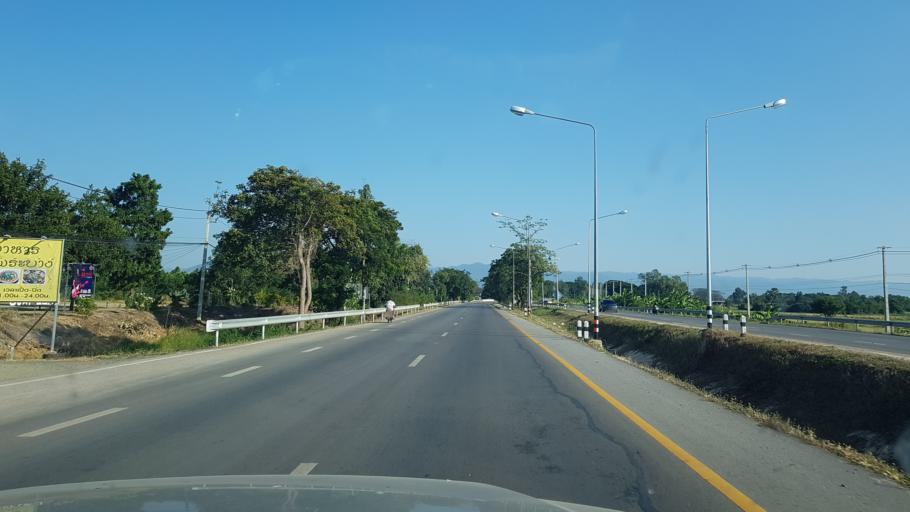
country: TH
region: Phetchabun
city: Lom Sak
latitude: 16.7371
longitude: 101.2312
